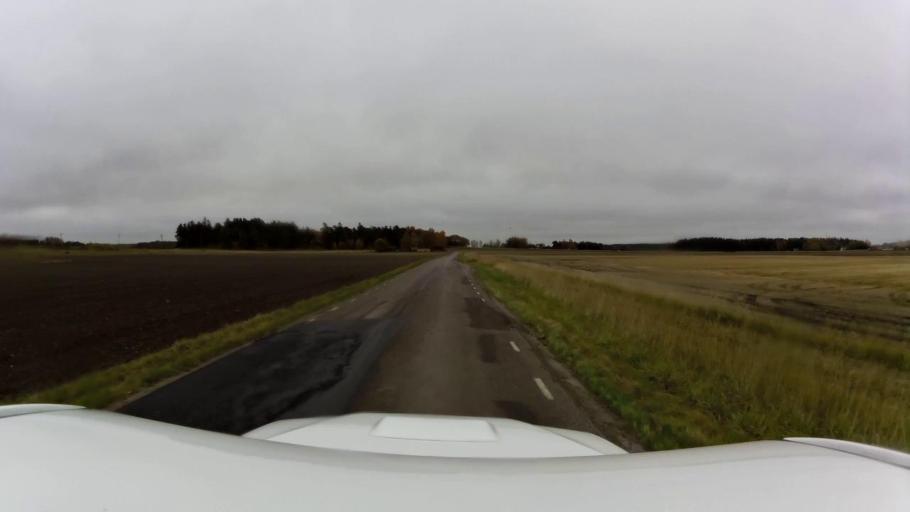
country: SE
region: OEstergoetland
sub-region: Linkopings Kommun
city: Linghem
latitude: 58.4354
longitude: 15.7167
